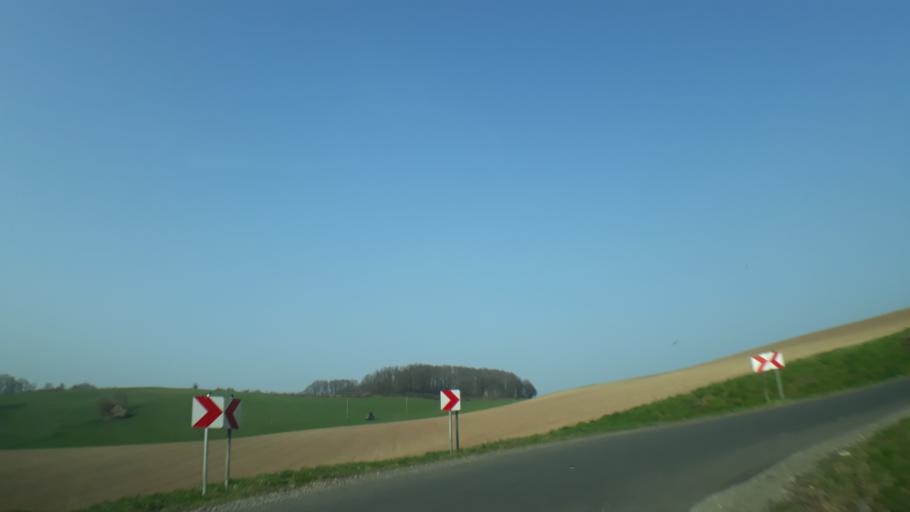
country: DE
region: North Rhine-Westphalia
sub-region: Regierungsbezirk Koln
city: Bad Munstereifel
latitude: 50.5398
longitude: 6.7316
